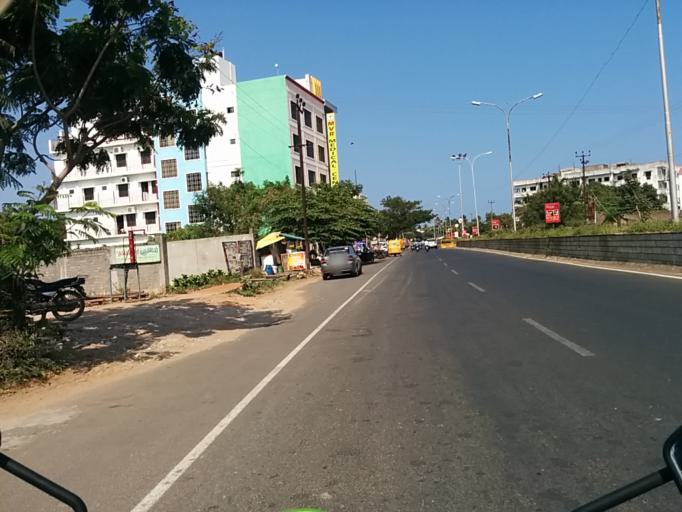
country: IN
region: Pondicherry
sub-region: Puducherry
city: Puducherry
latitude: 11.9545
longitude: 79.8221
